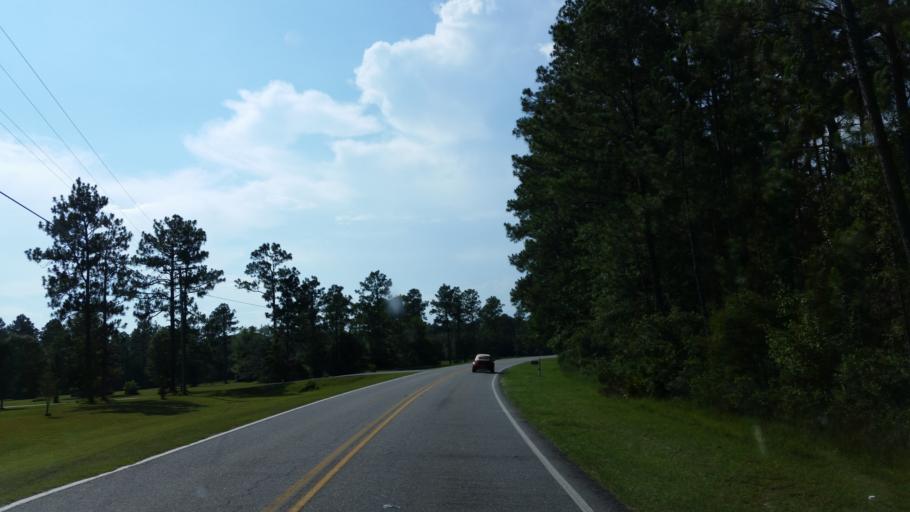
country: US
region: Georgia
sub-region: Lowndes County
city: Hahira
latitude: 30.9023
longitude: -83.3794
